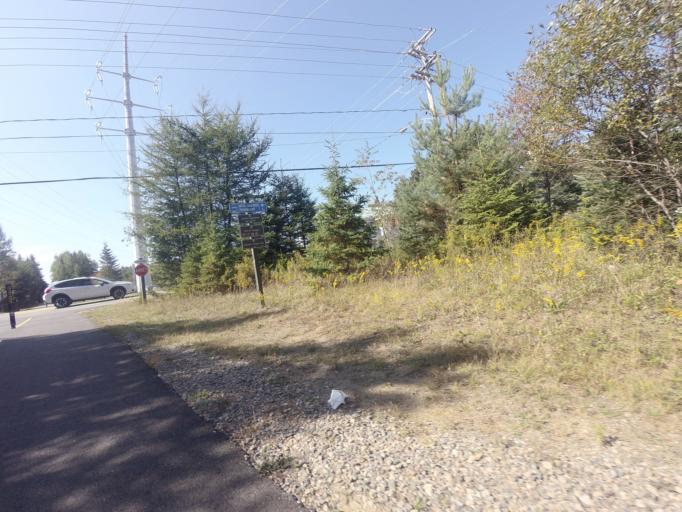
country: CA
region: Quebec
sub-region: Laurentides
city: Mont-Tremblant
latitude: 46.1290
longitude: -74.5562
